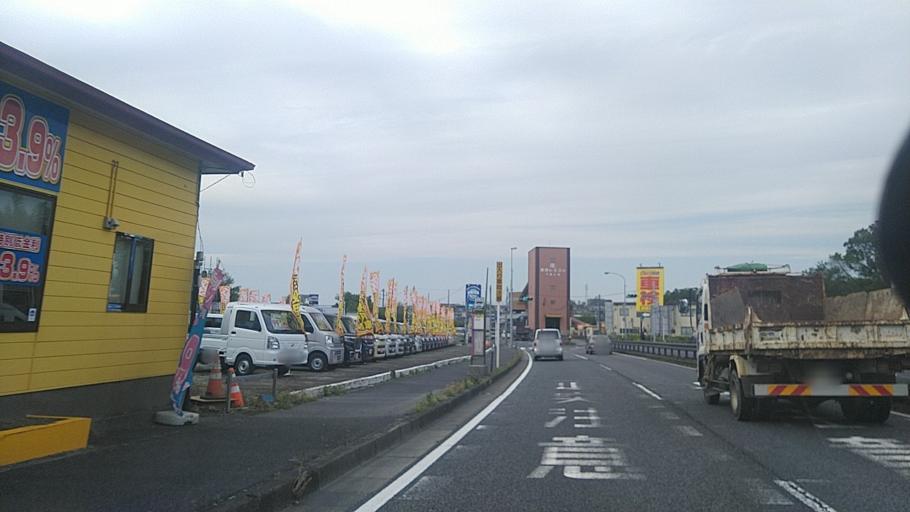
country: JP
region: Chiba
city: Yotsukaido
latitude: 35.7045
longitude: 140.1198
